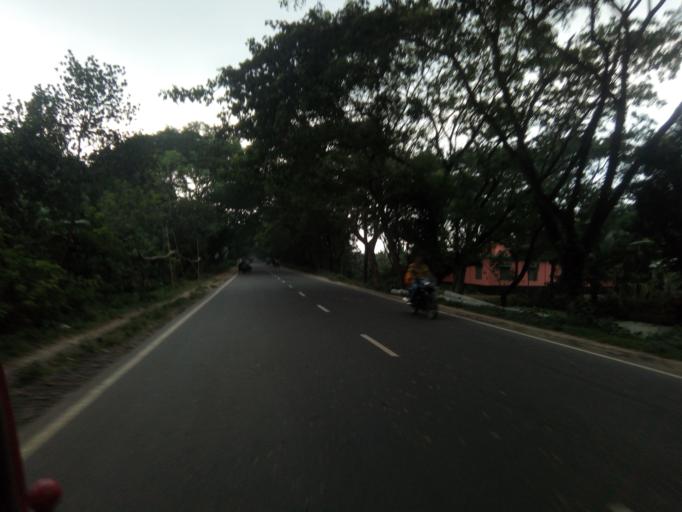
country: BD
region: Khulna
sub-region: Magura
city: Magura
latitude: 23.5397
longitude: 89.6204
